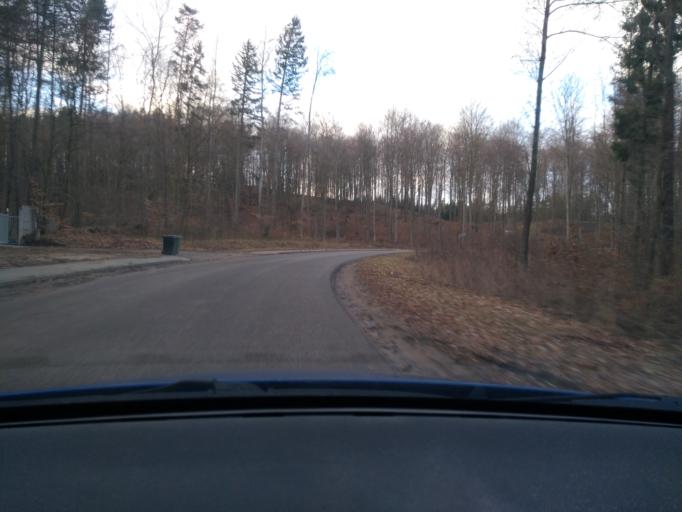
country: PL
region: Pomeranian Voivodeship
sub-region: Powiat kartuski
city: Kartuzy
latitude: 54.3587
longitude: 18.2175
